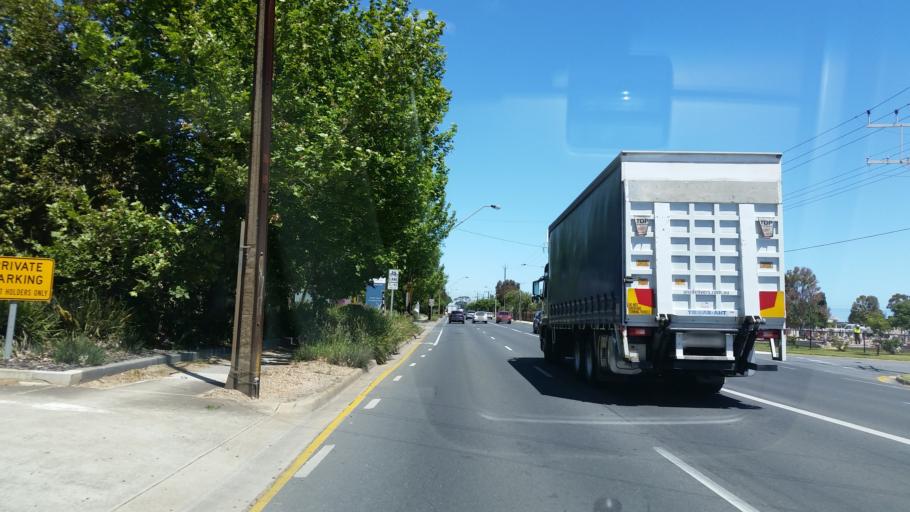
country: AU
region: South Australia
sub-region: Charles Sturt
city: Albert Park
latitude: -34.8705
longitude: 138.5288
